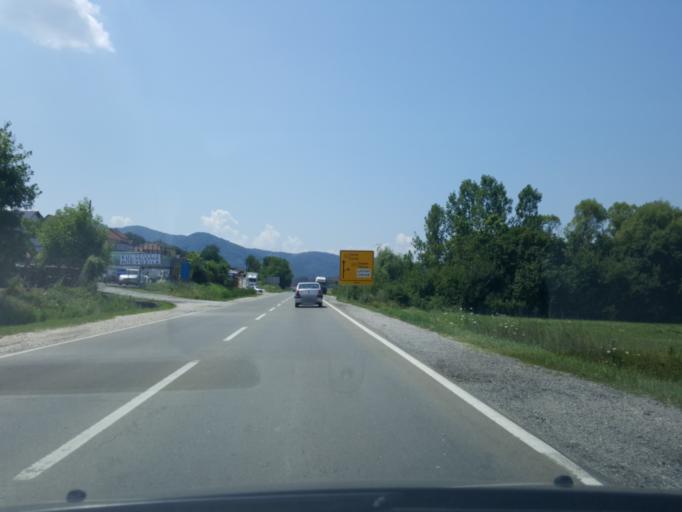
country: RS
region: Central Serbia
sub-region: Moravicki Okrug
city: Gornji Milanovac
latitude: 44.0257
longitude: 20.4686
